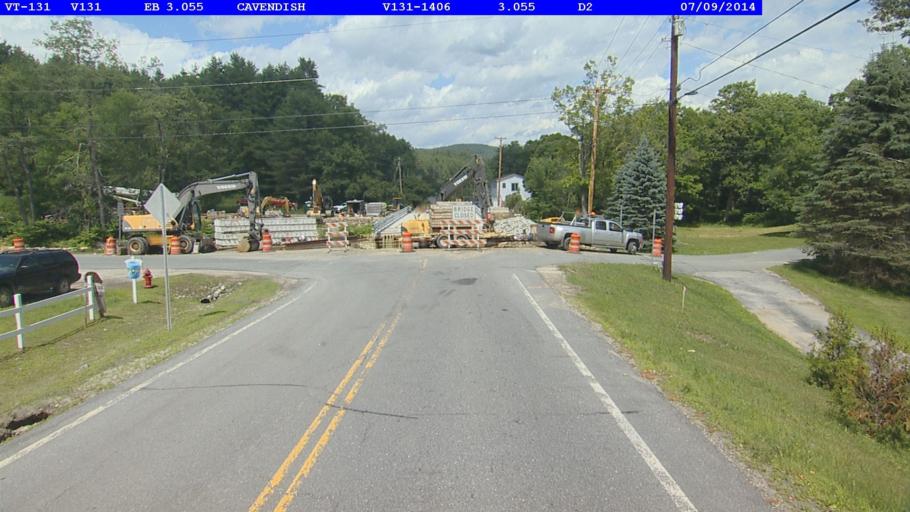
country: US
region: Vermont
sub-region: Windsor County
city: Chester
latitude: 43.3917
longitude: -72.5947
